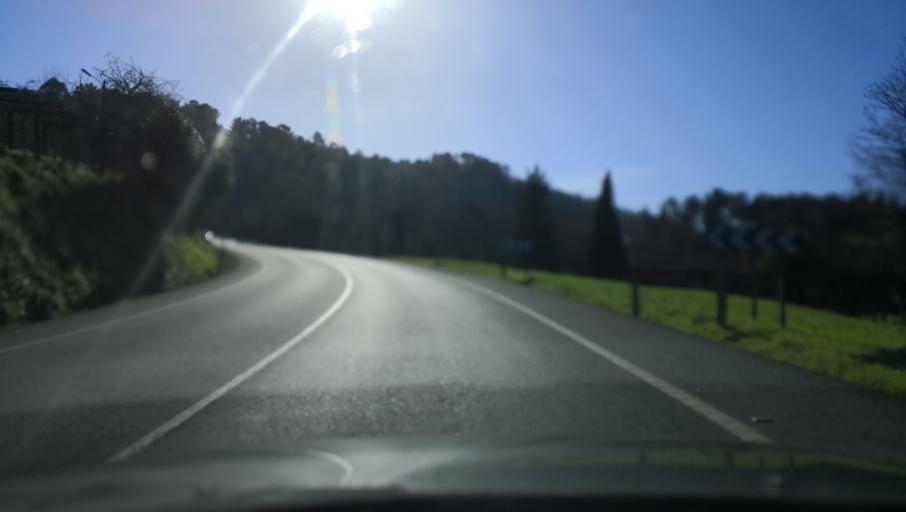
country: ES
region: Galicia
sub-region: Provincia da Coruna
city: Ribeira
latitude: 42.7720
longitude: -8.4000
